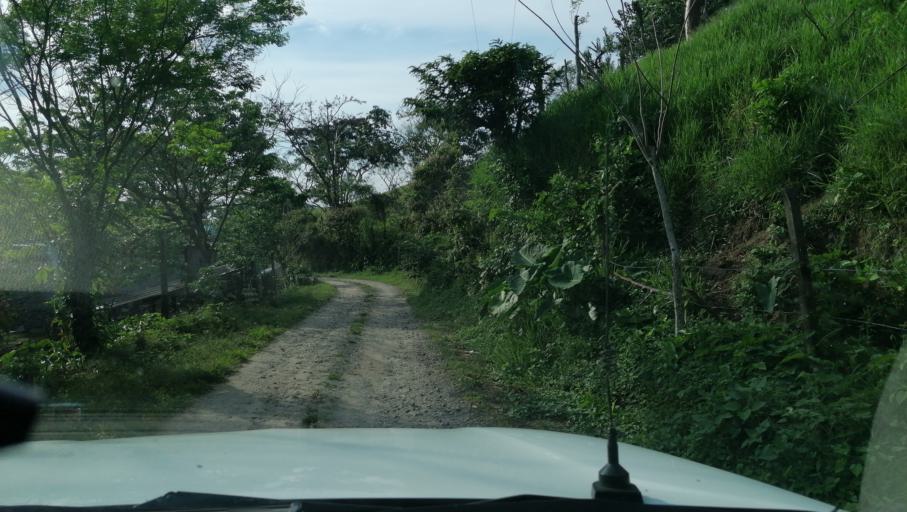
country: MX
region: Chiapas
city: Pichucalco
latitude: 17.4826
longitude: -93.2233
